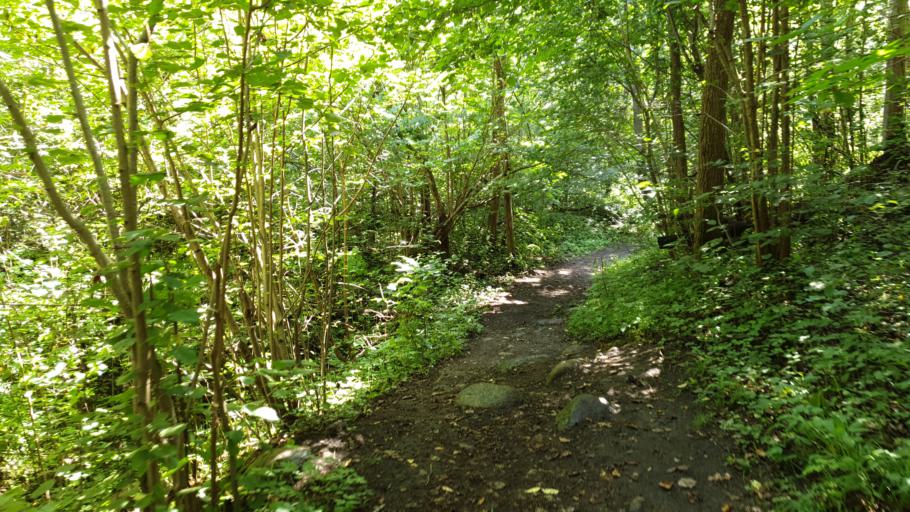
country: LT
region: Vilnius County
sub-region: Vilniaus Rajonas
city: Vievis
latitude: 54.8226
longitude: 24.9381
